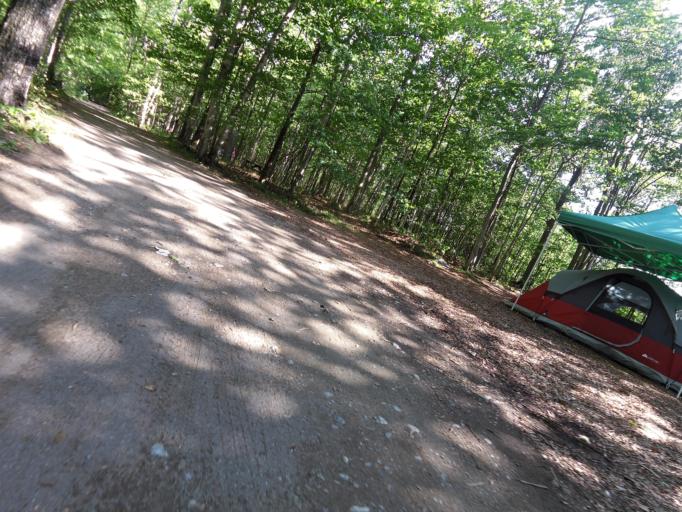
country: CA
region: Ontario
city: Tobermory
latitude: 45.2285
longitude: -81.6466
